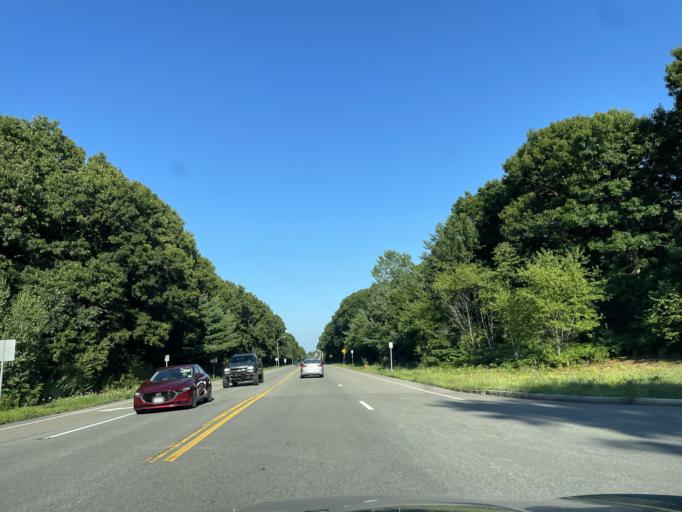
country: US
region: Massachusetts
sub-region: Bristol County
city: Easton
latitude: 42.0266
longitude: -71.1657
